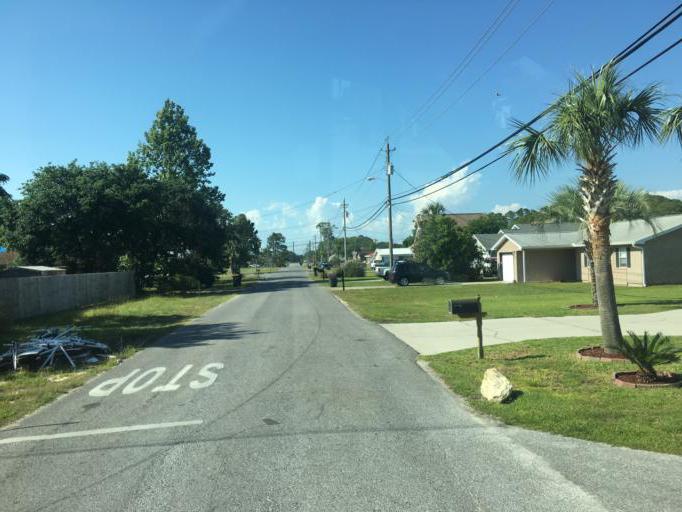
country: US
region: Florida
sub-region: Bay County
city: Panama City Beach
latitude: 30.2004
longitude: -85.8398
